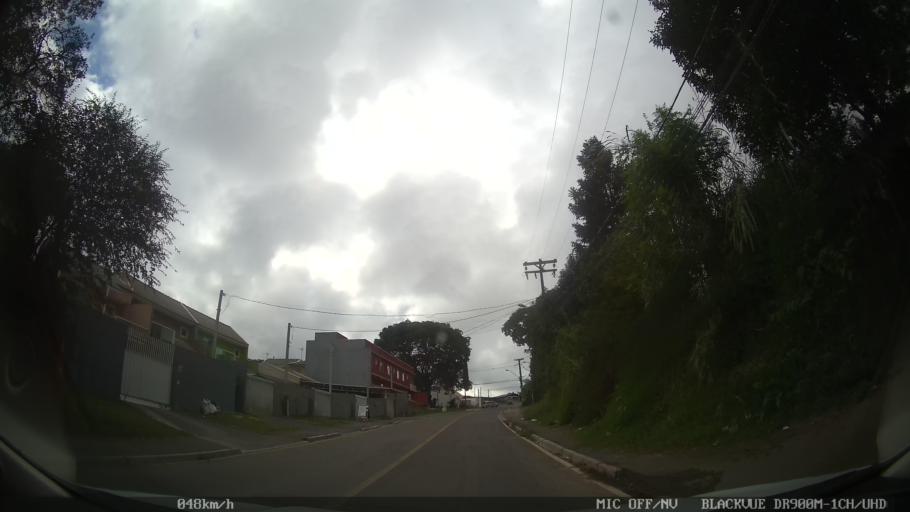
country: BR
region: Parana
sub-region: Colombo
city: Colombo
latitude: -25.3484
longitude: -49.2260
